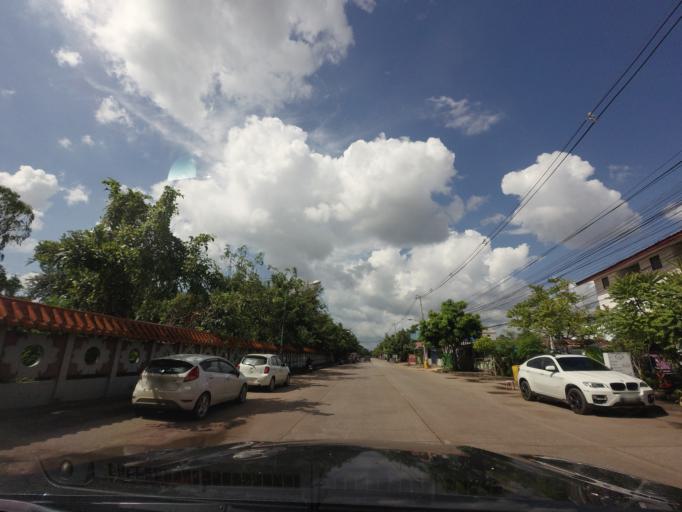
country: TH
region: Changwat Udon Thani
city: Udon Thani
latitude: 17.4165
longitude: 102.7769
